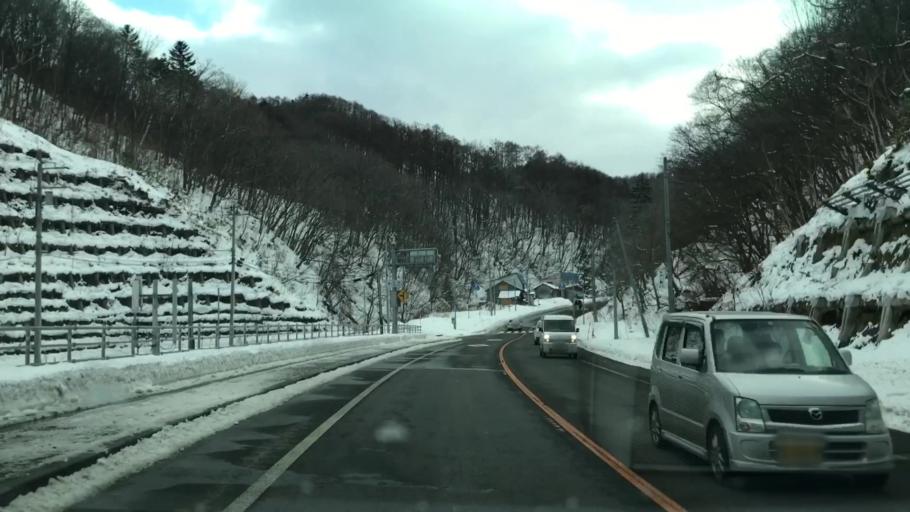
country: JP
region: Hokkaido
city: Yoichi
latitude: 43.2334
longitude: 140.7356
